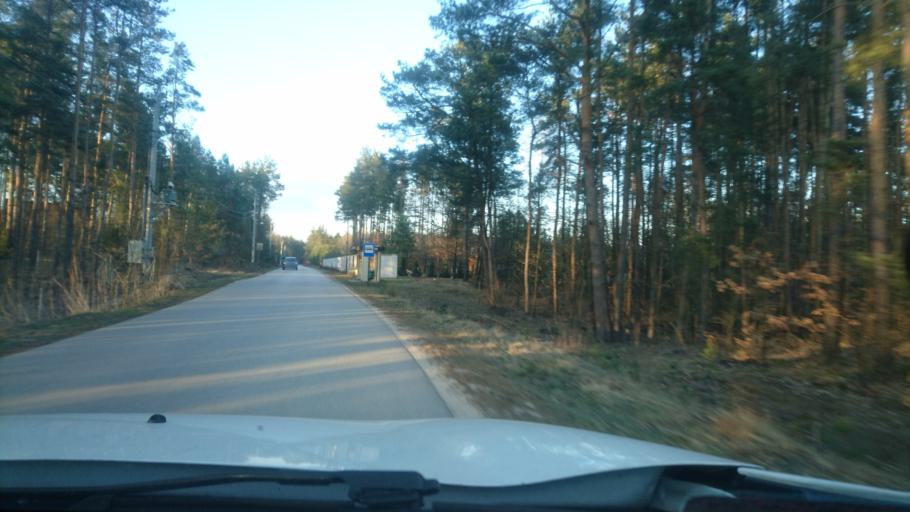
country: PL
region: Swietokrzyskie
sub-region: Powiat kielecki
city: Pierzchnica
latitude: 50.7794
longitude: 20.7126
